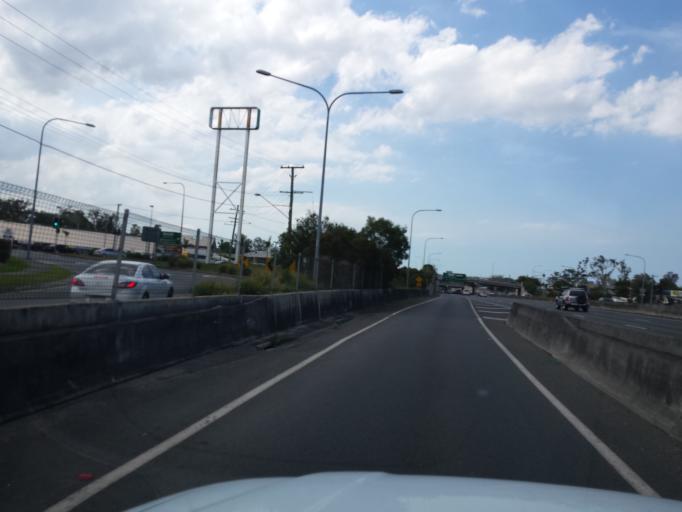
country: AU
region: Queensland
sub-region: Gold Coast
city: Nerang
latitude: -27.9995
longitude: 153.3395
